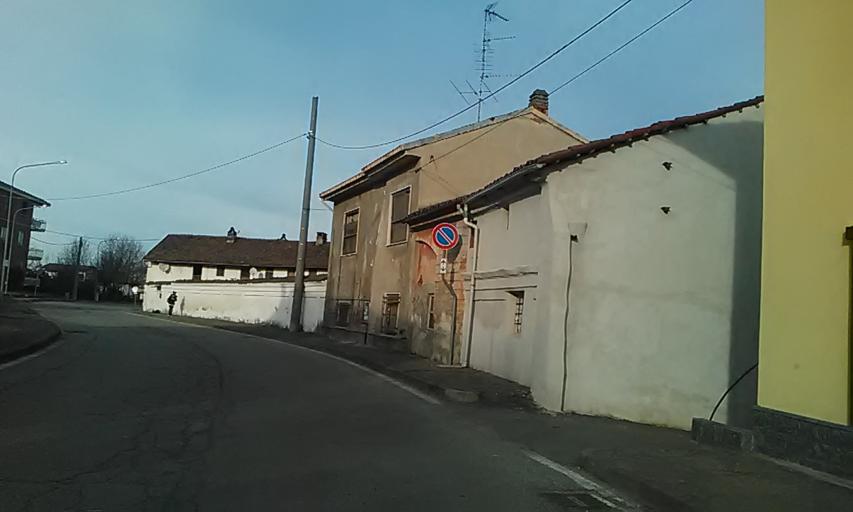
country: IT
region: Piedmont
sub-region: Provincia di Vercelli
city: Stroppiana
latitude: 45.2332
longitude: 8.4559
